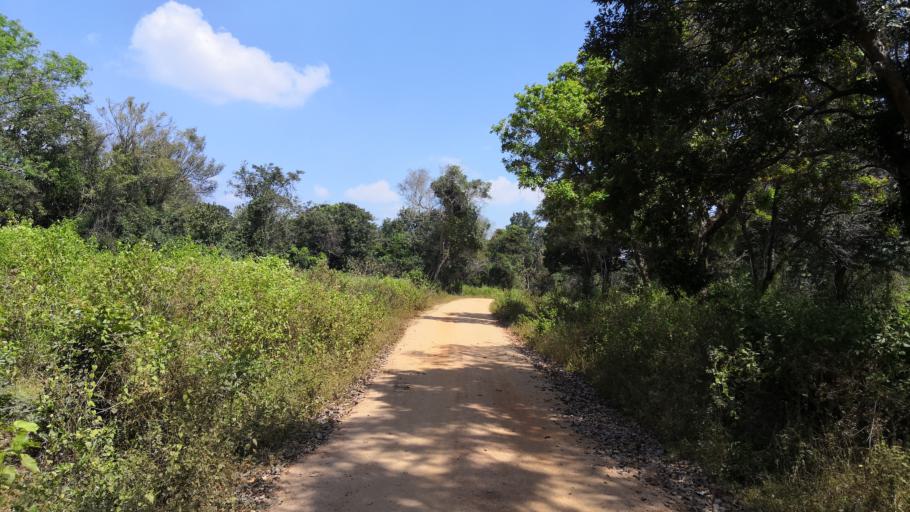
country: LK
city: Padaviya Divisional Secretariat
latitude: 8.9665
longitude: 80.6878
